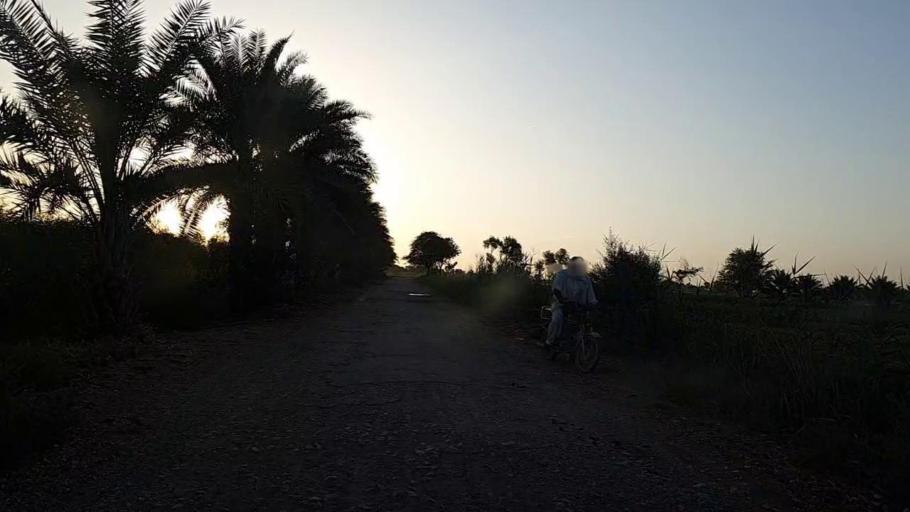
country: PK
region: Sindh
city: Hingorja
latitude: 27.0590
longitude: 68.3987
